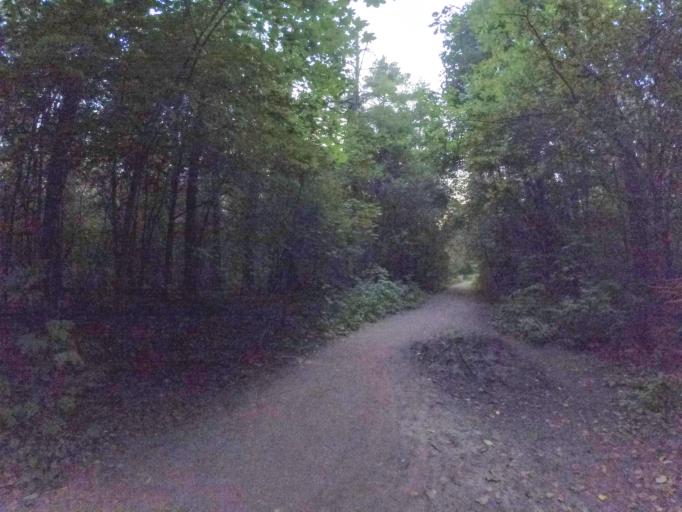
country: RU
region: Moskovskaya
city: Kotel'niki
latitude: 55.6659
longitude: 37.8453
